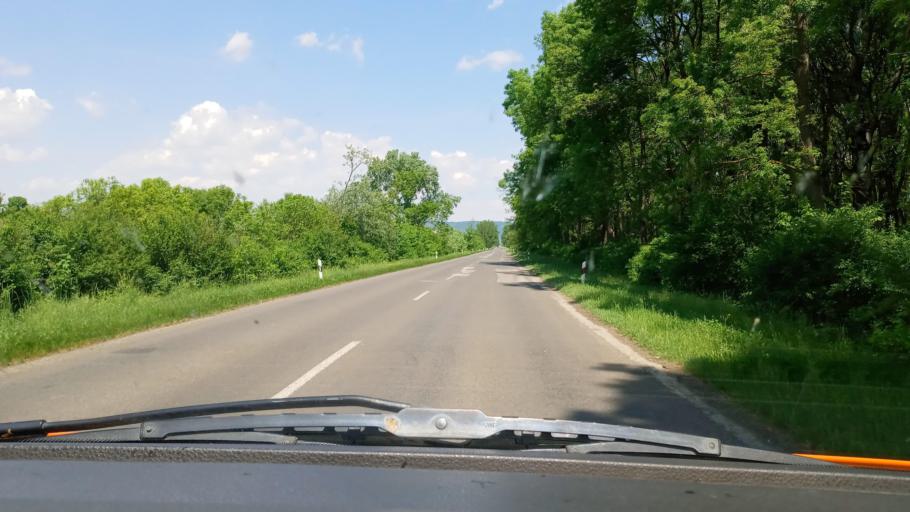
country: HU
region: Baranya
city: Harkany
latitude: 45.8201
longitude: 18.2168
